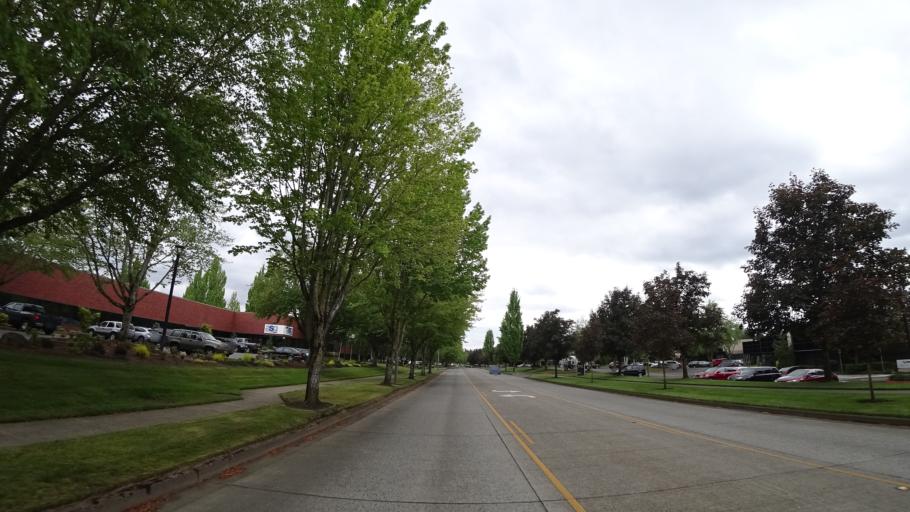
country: US
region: Oregon
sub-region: Washington County
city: Tigard
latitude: 45.4526
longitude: -122.7890
